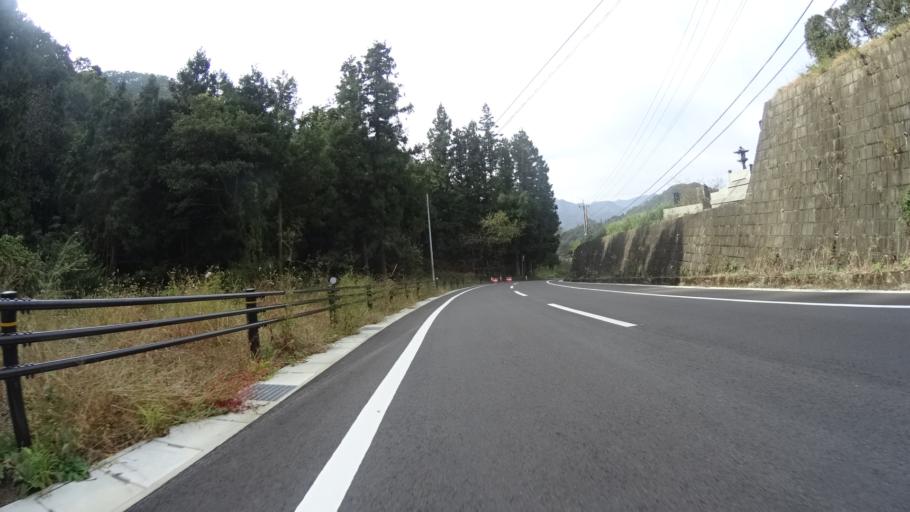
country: JP
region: Yamanashi
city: Otsuki
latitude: 35.6162
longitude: 139.0177
